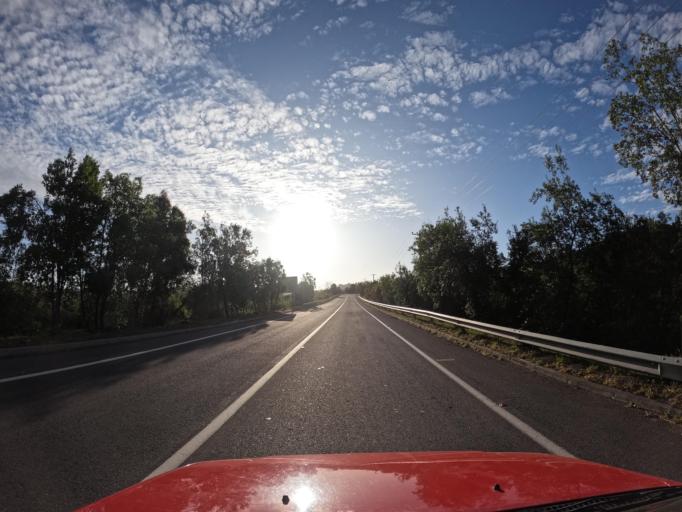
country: CL
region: Valparaiso
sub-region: San Antonio Province
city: San Antonio
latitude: -34.0509
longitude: -71.6027
